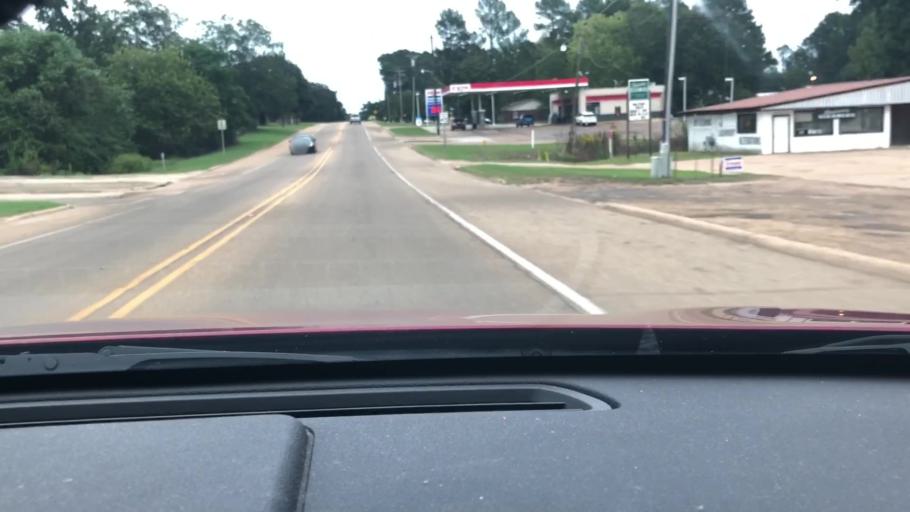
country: US
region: Arkansas
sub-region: Lafayette County
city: Stamps
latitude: 33.3652
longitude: -93.4855
